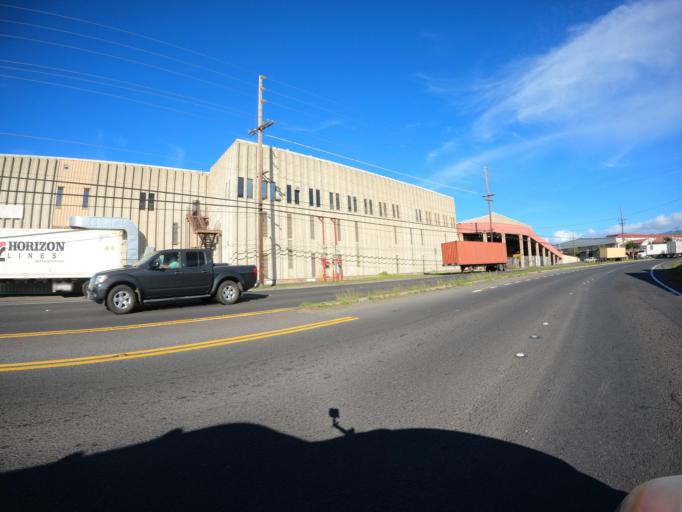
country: US
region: Hawaii
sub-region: Honolulu County
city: Honolulu
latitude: 21.3220
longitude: -157.8917
